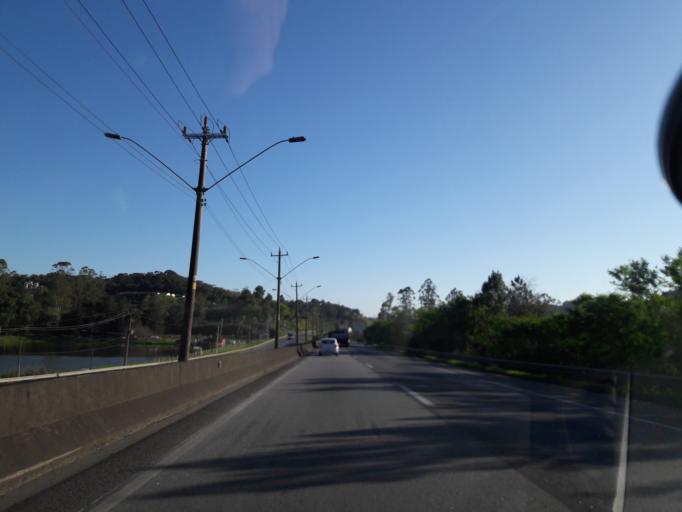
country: BR
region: Sao Paulo
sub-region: Sao Lourenco Da Serra
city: Sao Lourenco da Serra
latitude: -23.8753
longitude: -46.9667
